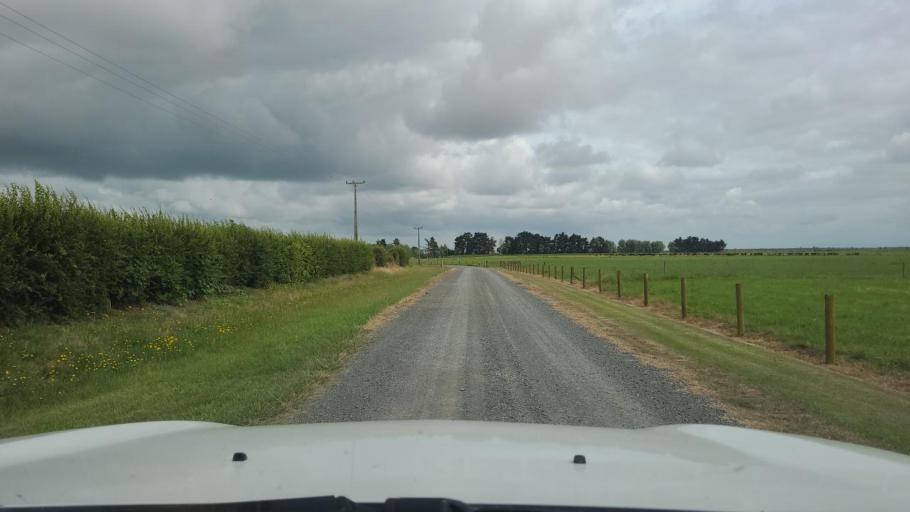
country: NZ
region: Waikato
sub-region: Hauraki District
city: Paeroa
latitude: -37.5072
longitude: 175.5882
